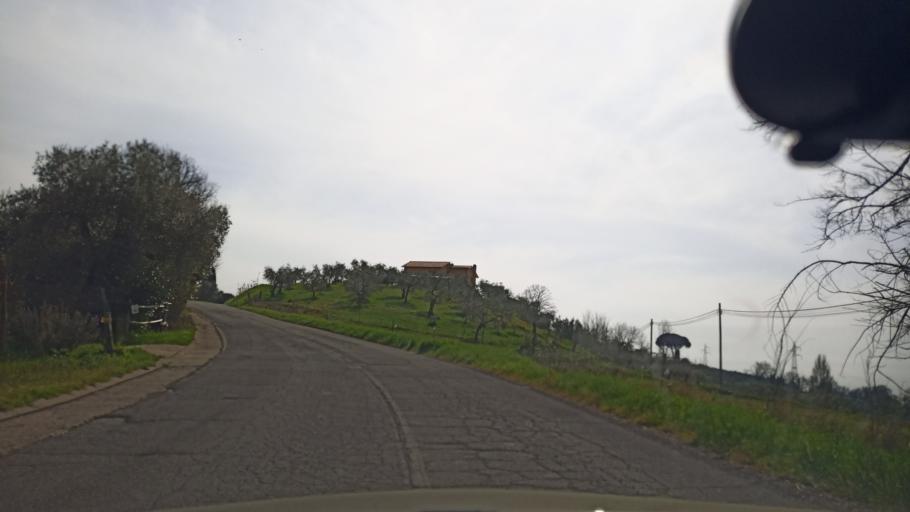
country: IT
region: Latium
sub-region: Provincia di Rieti
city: Torri in Sabina
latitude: 42.3554
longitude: 12.6505
